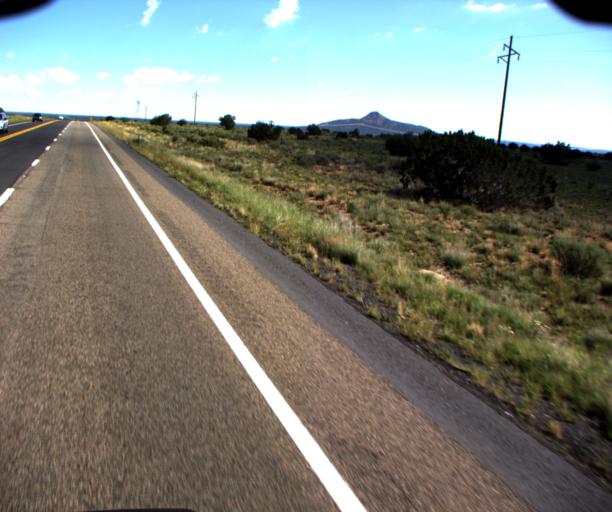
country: US
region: Arizona
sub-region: Coconino County
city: Grand Canyon Village
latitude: 35.7549
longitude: -112.1309
